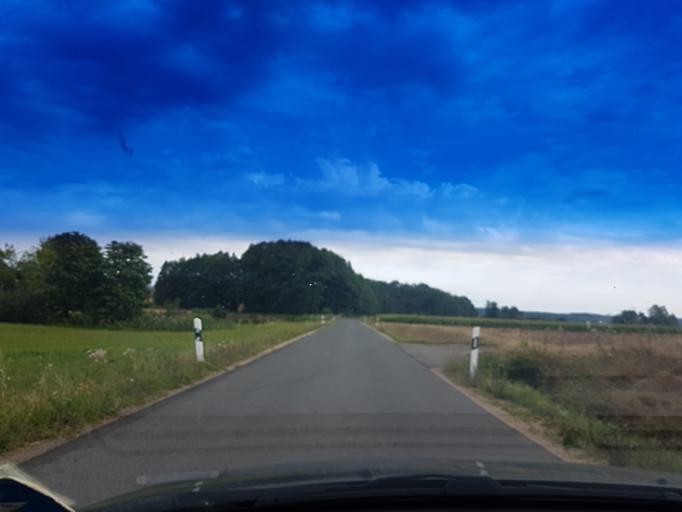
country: DE
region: Bavaria
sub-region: Upper Franconia
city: Frensdorf
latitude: 49.8314
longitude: 10.8622
